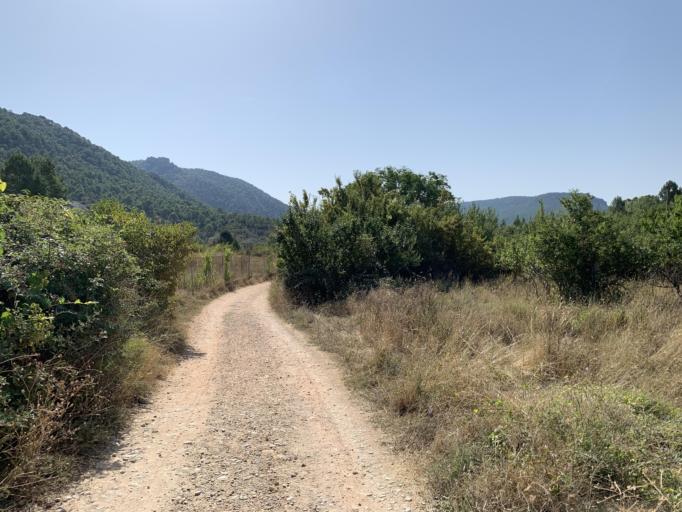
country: ES
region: Castille-La Mancha
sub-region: Provincia de Guadalajara
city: Ocentejo
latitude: 40.7664
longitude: -2.3955
